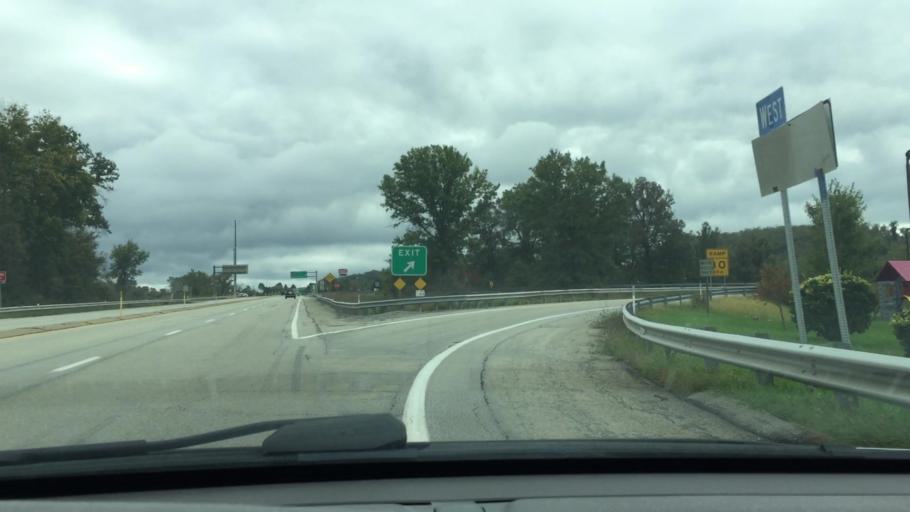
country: US
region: Pennsylvania
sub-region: Westmoreland County
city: Fellsburg
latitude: 40.1571
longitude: -79.7774
